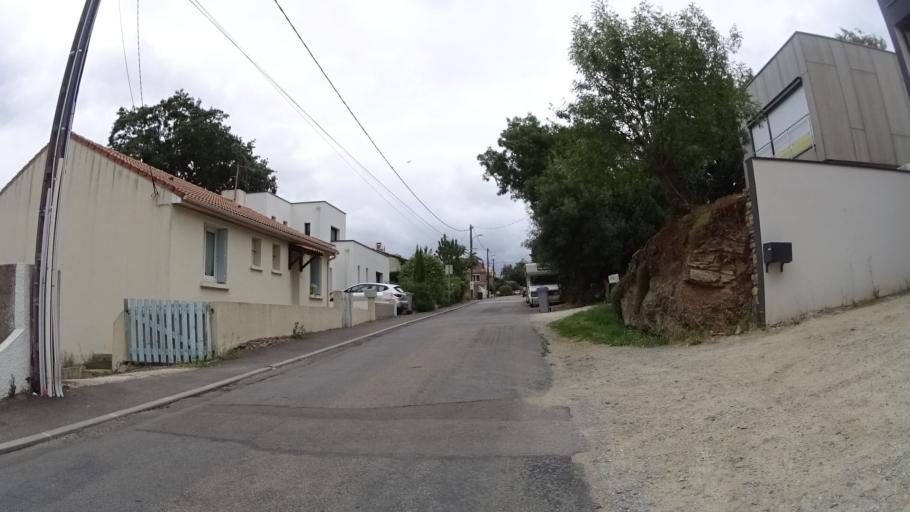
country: FR
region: Pays de la Loire
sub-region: Departement de la Loire-Atlantique
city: Le Pellerin
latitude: 47.1998
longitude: -1.7416
